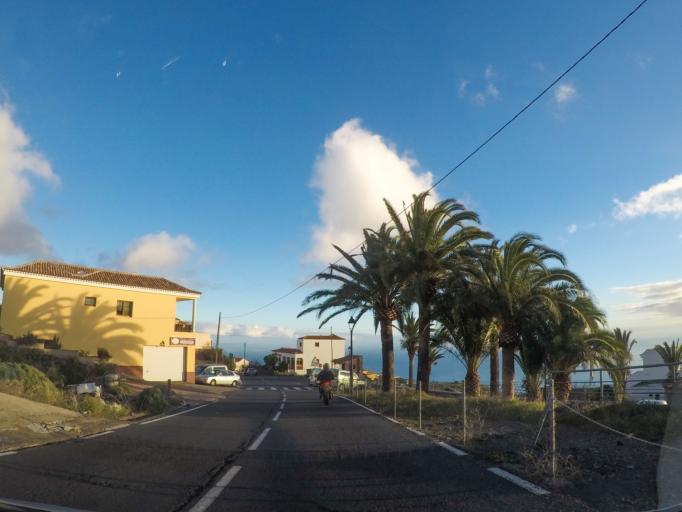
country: ES
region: Canary Islands
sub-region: Provincia de Santa Cruz de Tenerife
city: Alajero
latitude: 28.0579
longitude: -17.2345
